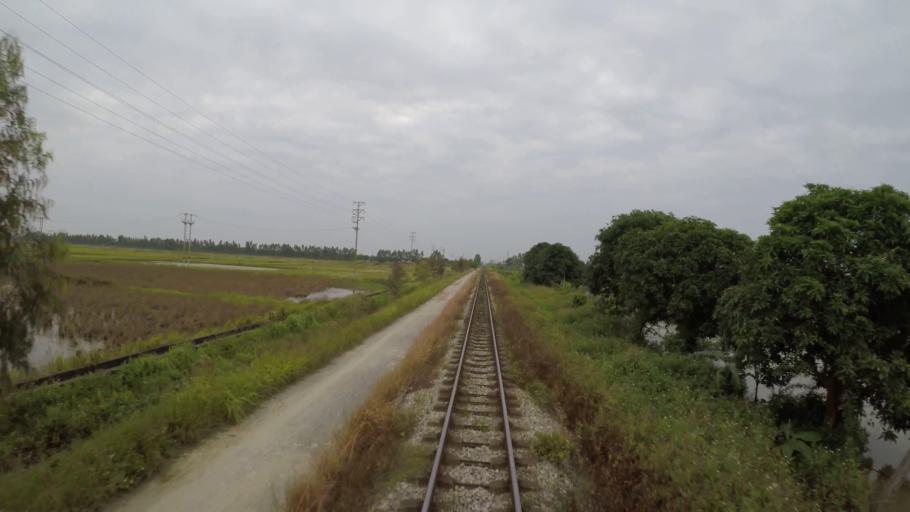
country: VN
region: Hai Duong
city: Lai Cach
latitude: 20.9478
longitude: 106.2570
